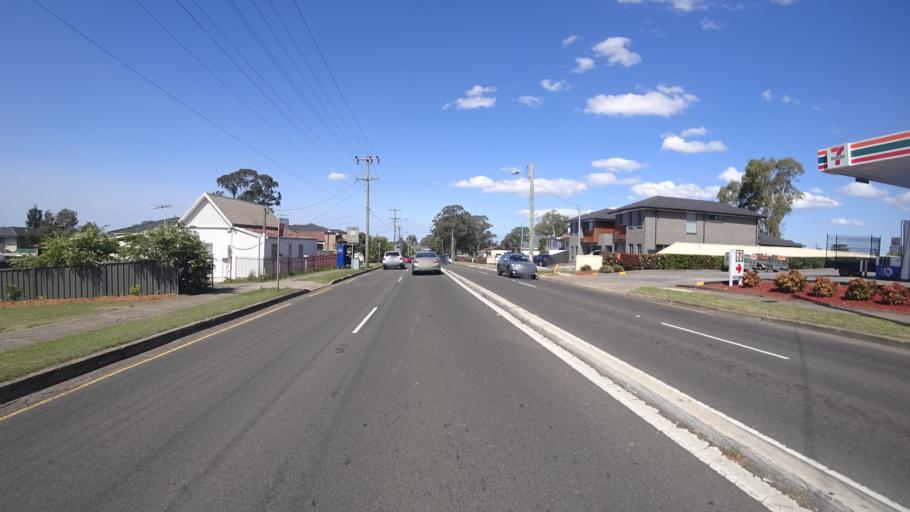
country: AU
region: New South Wales
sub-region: Fairfield
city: Cabramatta West
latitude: -33.8971
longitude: 150.9131
